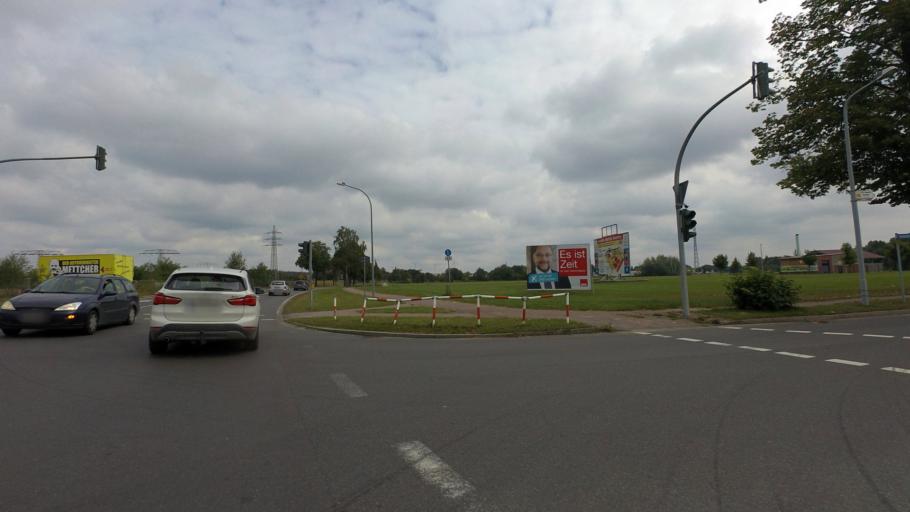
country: DE
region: Brandenburg
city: Finsterwalde
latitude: 51.6376
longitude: 13.7292
